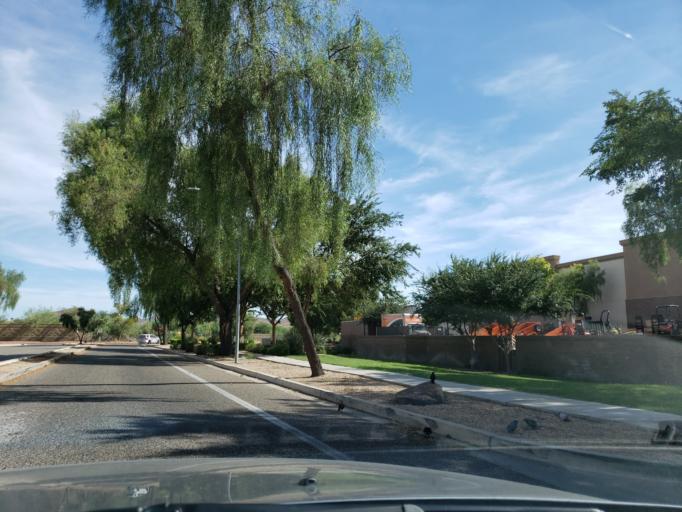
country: US
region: Arizona
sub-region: Maricopa County
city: Peoria
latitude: 33.6667
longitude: -112.1919
